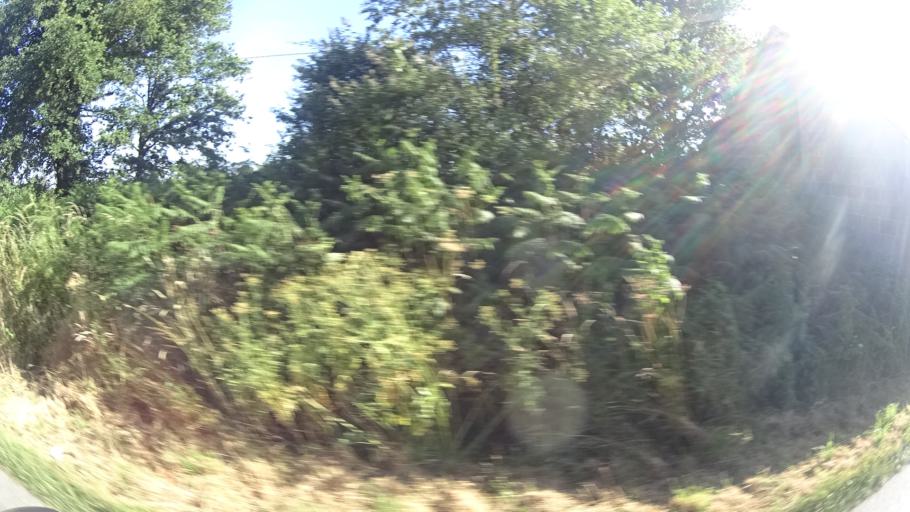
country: FR
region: Brittany
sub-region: Departement d'Ille-et-Vilaine
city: Grand-Fougeray
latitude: 47.7266
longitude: -1.7461
